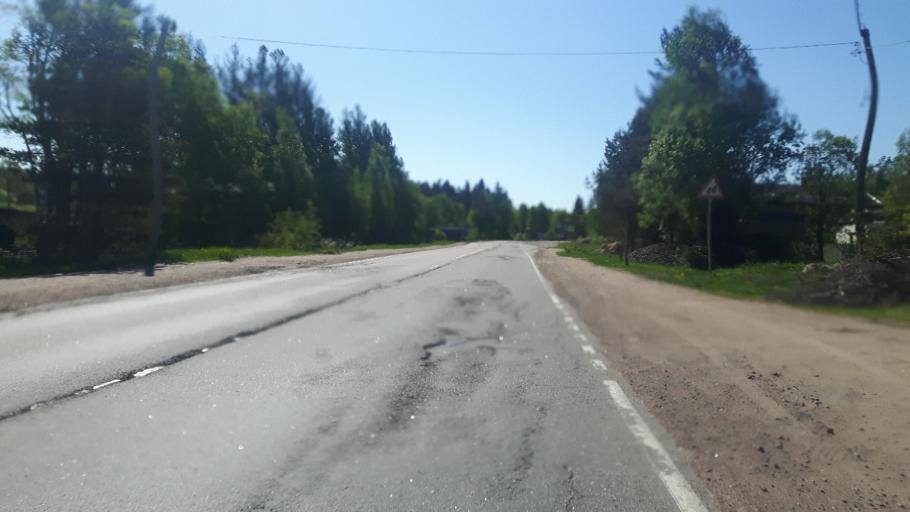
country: RU
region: Leningrad
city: Vyborg
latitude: 60.6500
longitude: 28.7473
